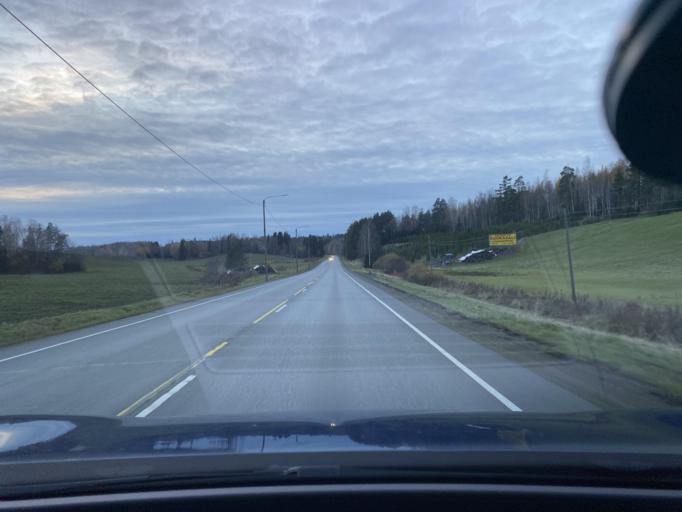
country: FI
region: Uusimaa
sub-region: Helsinki
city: Saukkola
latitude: 60.3884
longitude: 24.0445
